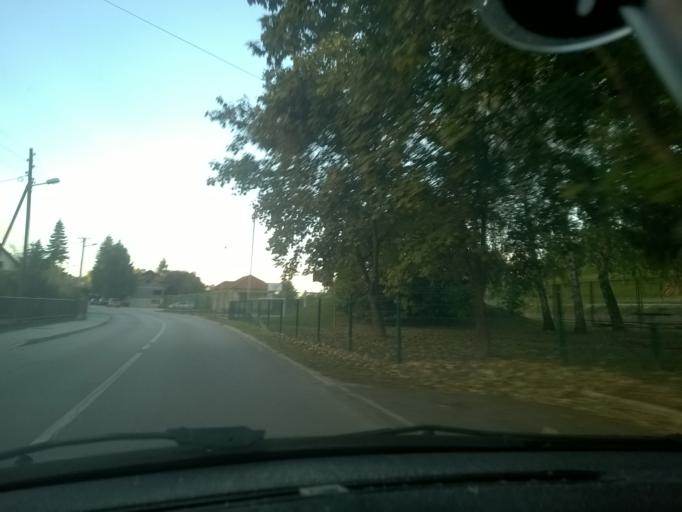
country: HR
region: Krapinsko-Zagorska
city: Zabok
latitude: 46.0347
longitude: 15.9108
